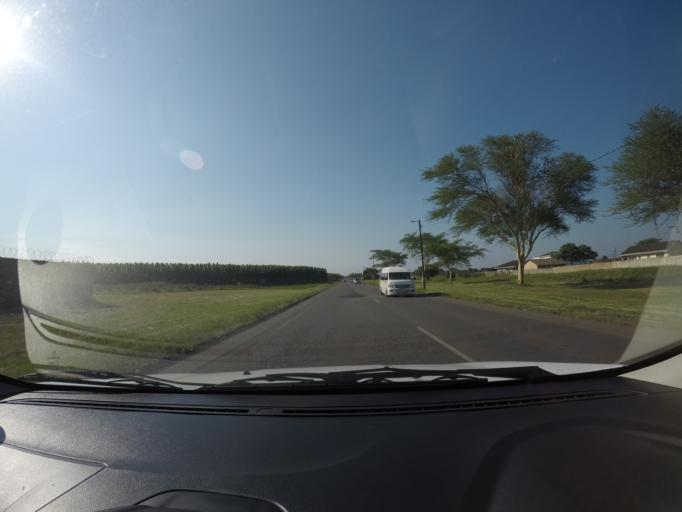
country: ZA
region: KwaZulu-Natal
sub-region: uThungulu District Municipality
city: Richards Bay
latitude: -28.7230
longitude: 32.0344
